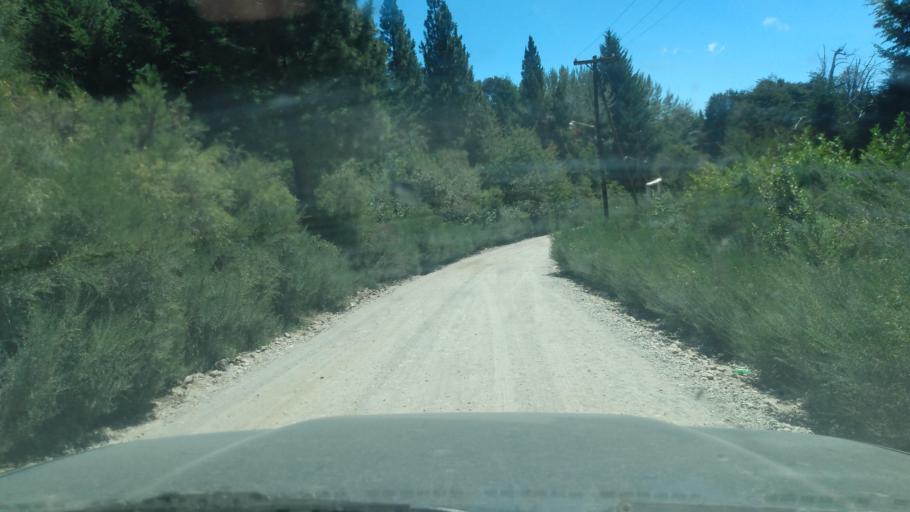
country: AR
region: Rio Negro
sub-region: Departamento de Bariloche
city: San Carlos de Bariloche
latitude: -41.0968
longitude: -71.5189
